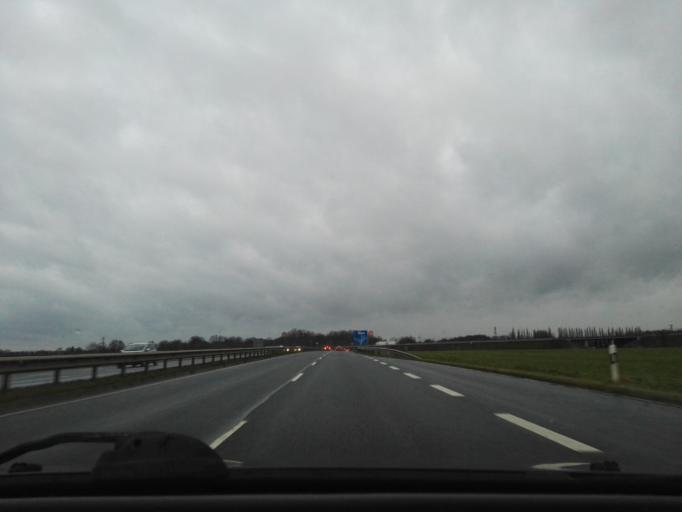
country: DE
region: Lower Saxony
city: Lengede
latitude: 52.1492
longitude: 10.3655
